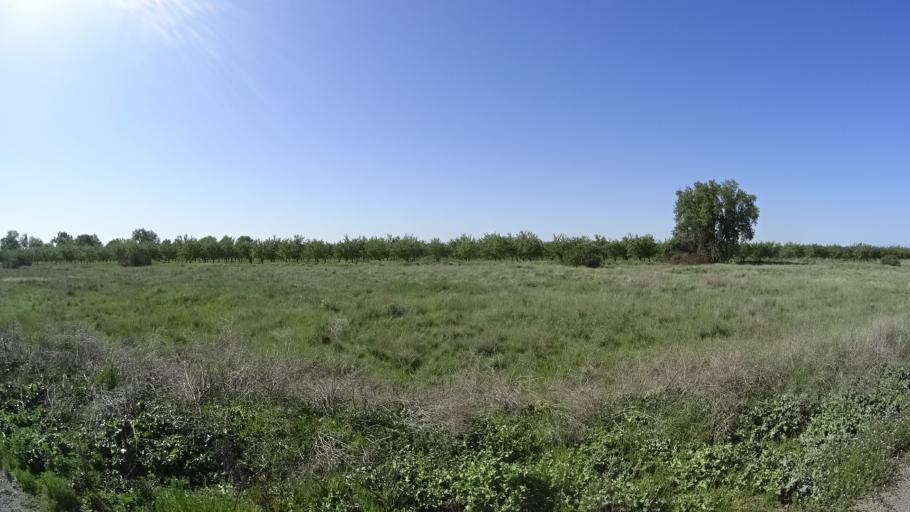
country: US
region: California
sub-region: Glenn County
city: Hamilton City
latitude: 39.7130
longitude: -121.9821
